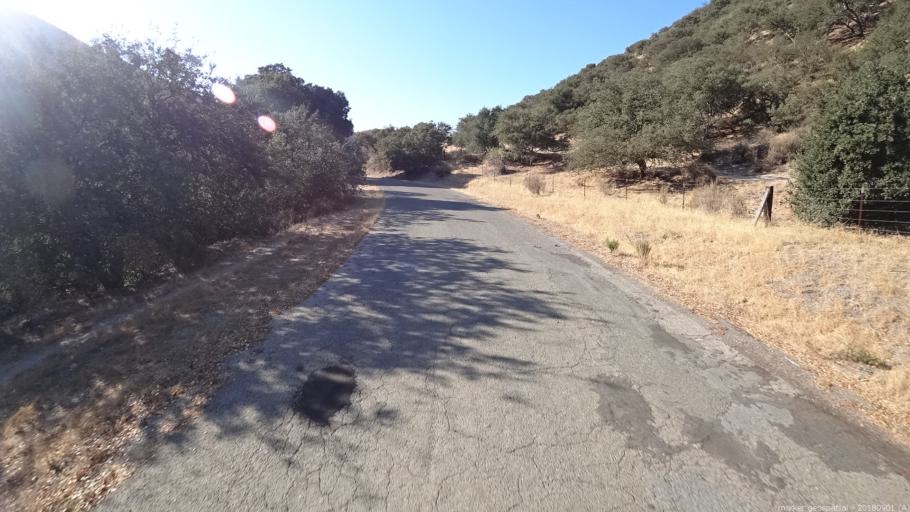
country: US
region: California
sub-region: Monterey County
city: Greenfield
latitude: 36.2243
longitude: -121.2798
